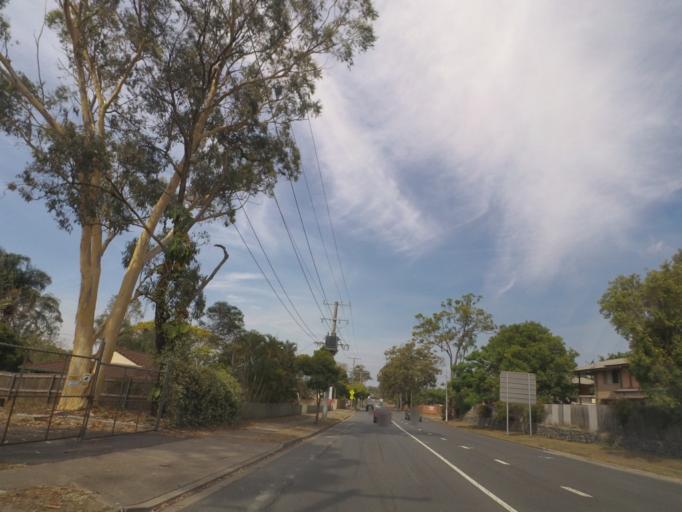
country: AU
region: Queensland
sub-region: Brisbane
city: Sunnybank Hills
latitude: -27.5988
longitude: 153.0406
